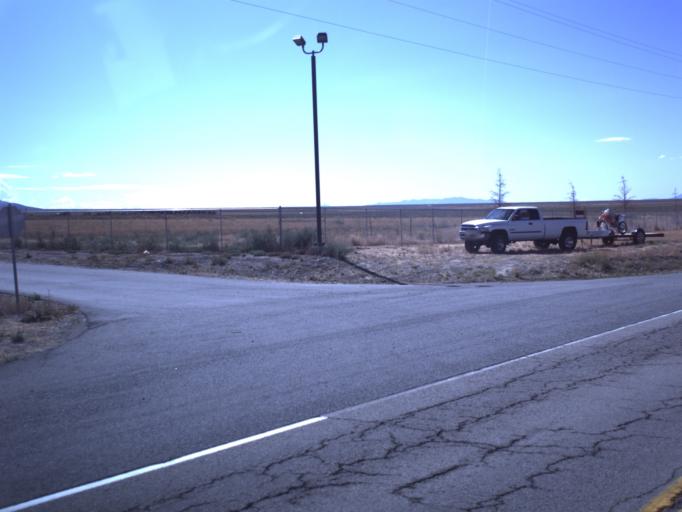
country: US
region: Utah
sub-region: Tooele County
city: Tooele
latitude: 40.4068
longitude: -112.3854
